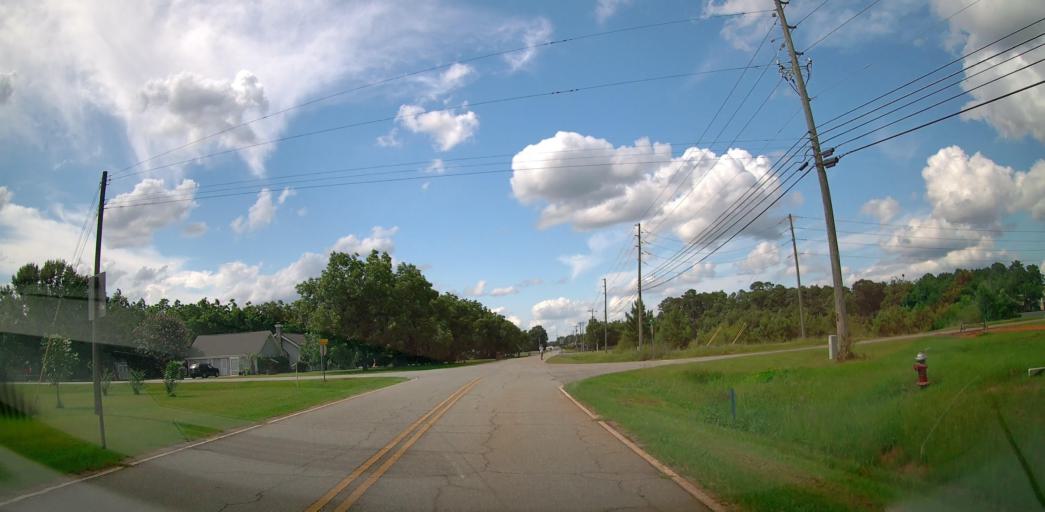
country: US
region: Georgia
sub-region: Houston County
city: Centerville
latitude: 32.5836
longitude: -83.6664
